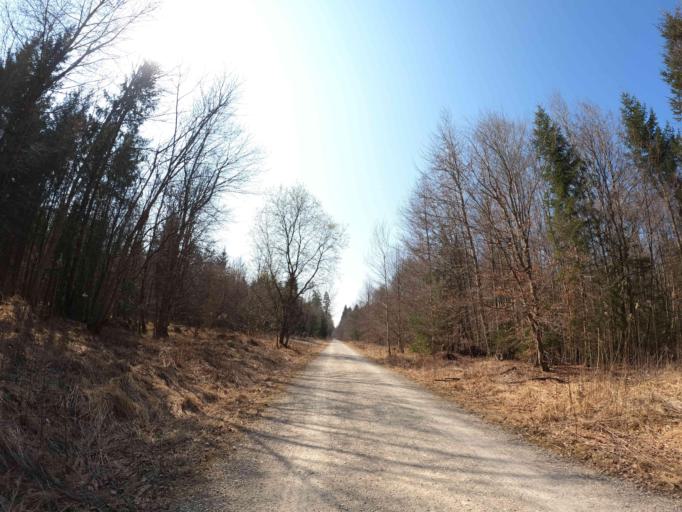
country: DE
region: Bavaria
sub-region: Upper Bavaria
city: Neuried
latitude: 48.0699
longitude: 11.4731
